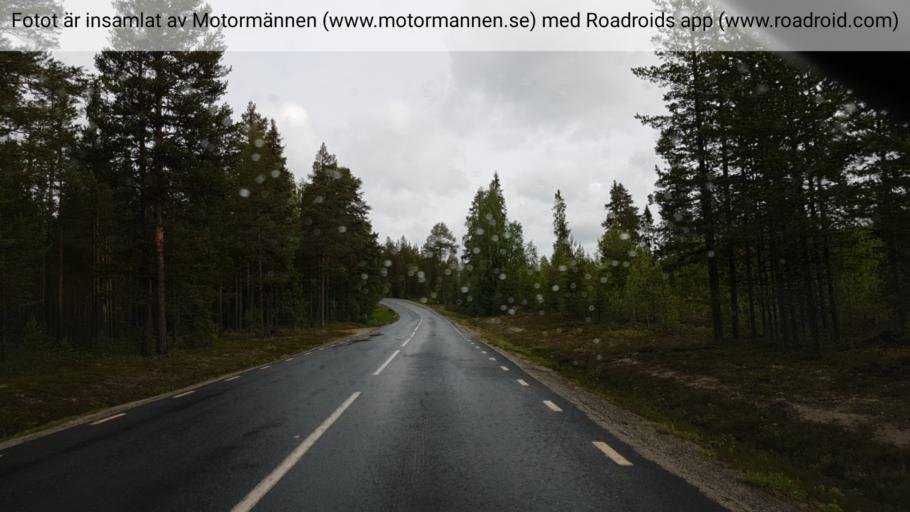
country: SE
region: Vaesterbotten
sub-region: Norsjo Kommun
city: Norsjoe
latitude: 64.6316
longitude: 19.2886
